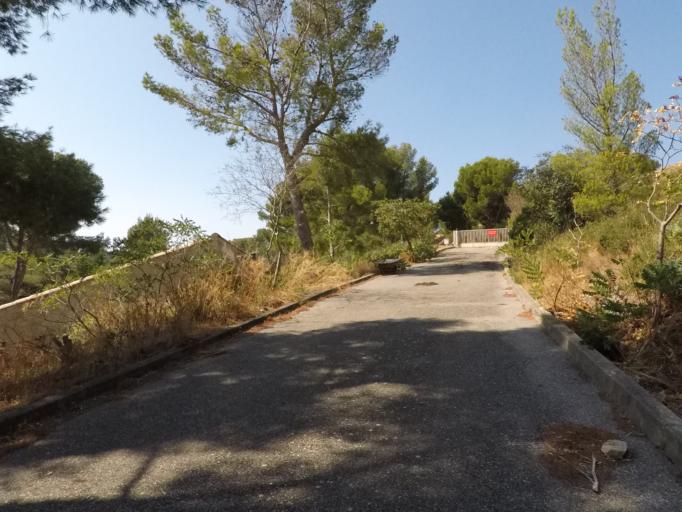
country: FR
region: Provence-Alpes-Cote d'Azur
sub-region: Departement des Bouches-du-Rhone
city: Marseille 10
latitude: 43.2559
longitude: 5.4400
